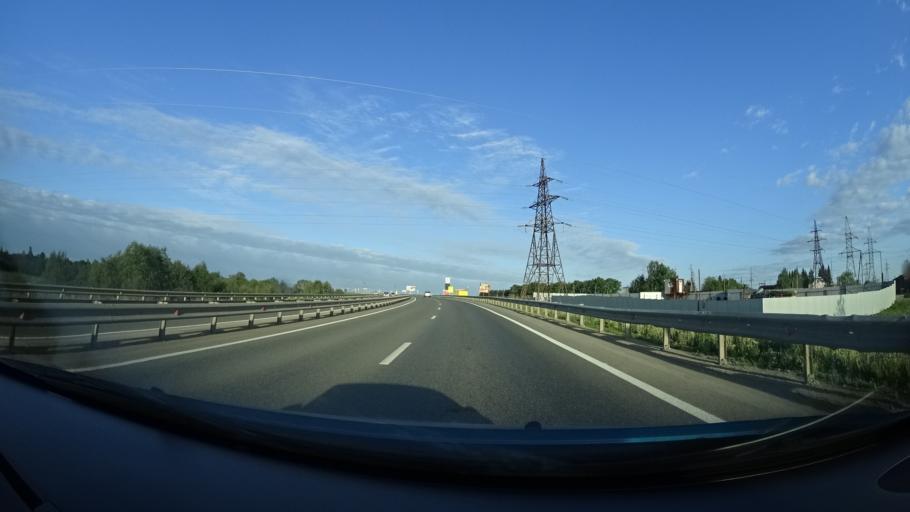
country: RU
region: Perm
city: Kultayevo
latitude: 57.8867
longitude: 55.9301
